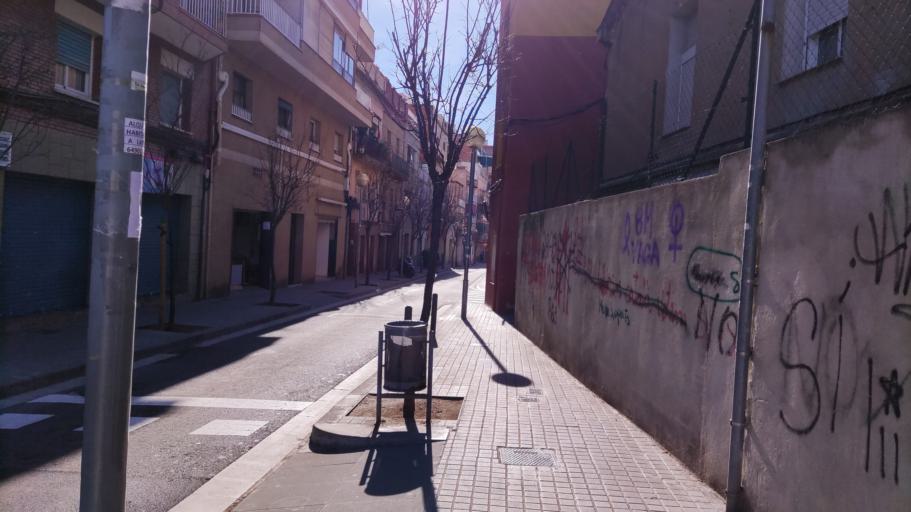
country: ES
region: Catalonia
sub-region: Provincia de Barcelona
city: Llefia
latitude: 41.4371
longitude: 2.2196
